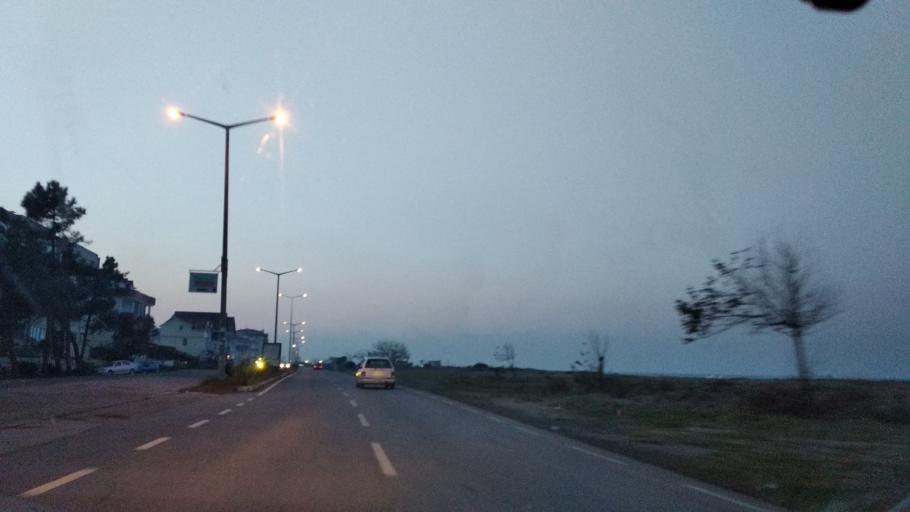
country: TR
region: Sakarya
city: Karasu
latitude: 41.0956
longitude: 30.7315
